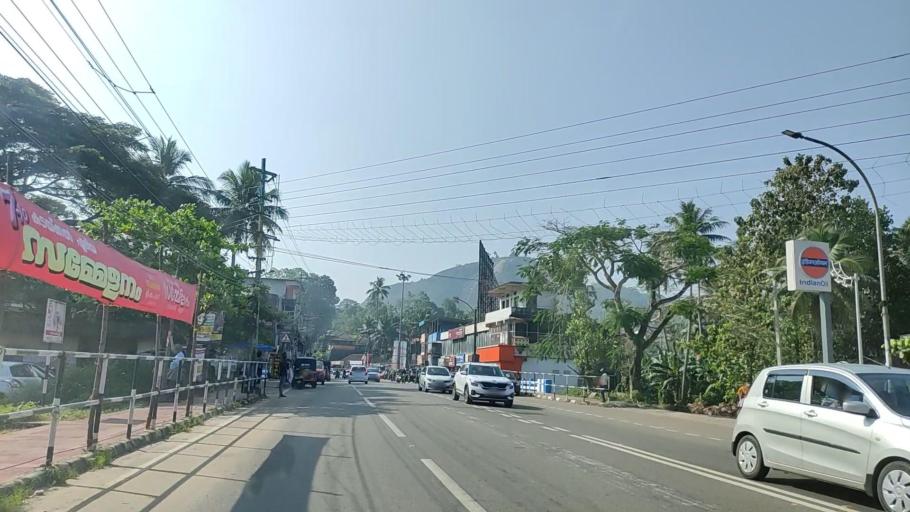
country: IN
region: Kerala
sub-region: Kollam
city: Punalur
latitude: 8.8741
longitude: 76.8694
